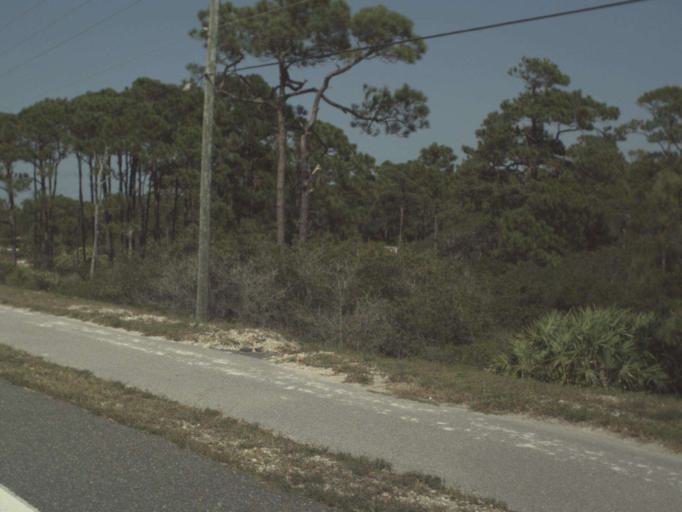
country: US
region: Florida
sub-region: Gulf County
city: Port Saint Joe
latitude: 29.7269
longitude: -85.3891
